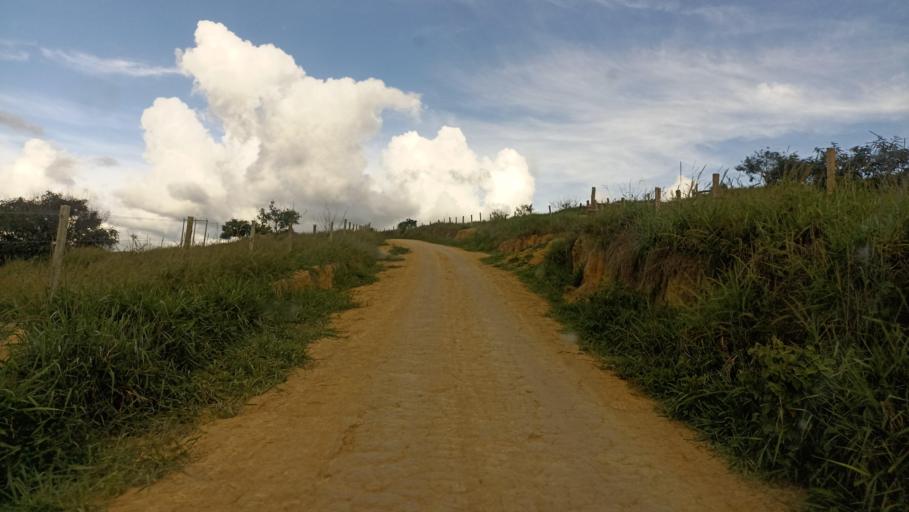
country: BR
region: Minas Gerais
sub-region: Almenara
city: Almenara
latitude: -16.5489
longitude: -40.4563
